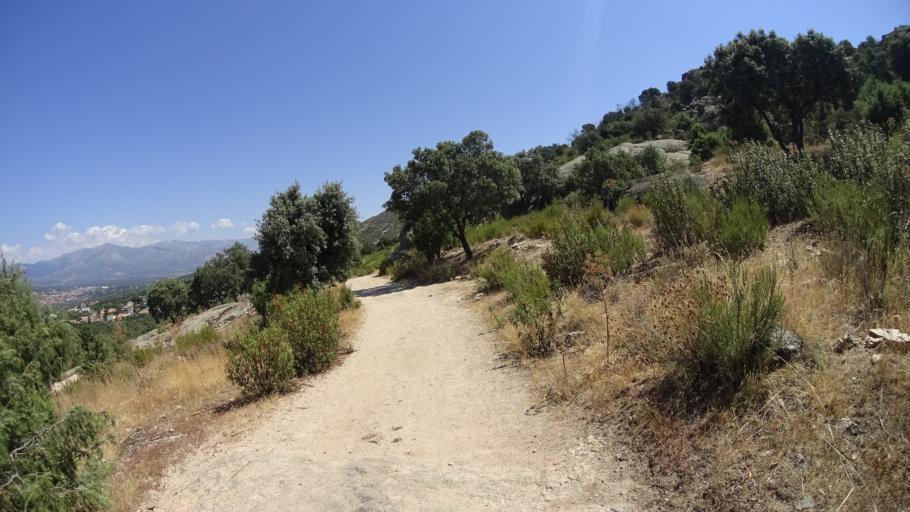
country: ES
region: Madrid
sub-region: Provincia de Madrid
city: Moralzarzal
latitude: 40.6406
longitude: -3.9659
